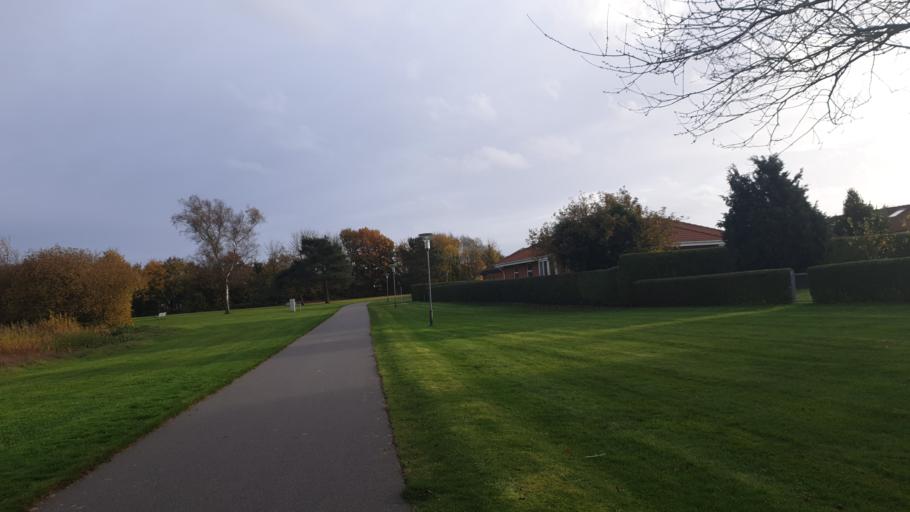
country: DK
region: Central Jutland
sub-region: Hedensted Kommune
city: Hedensted
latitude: 55.7937
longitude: 9.6947
